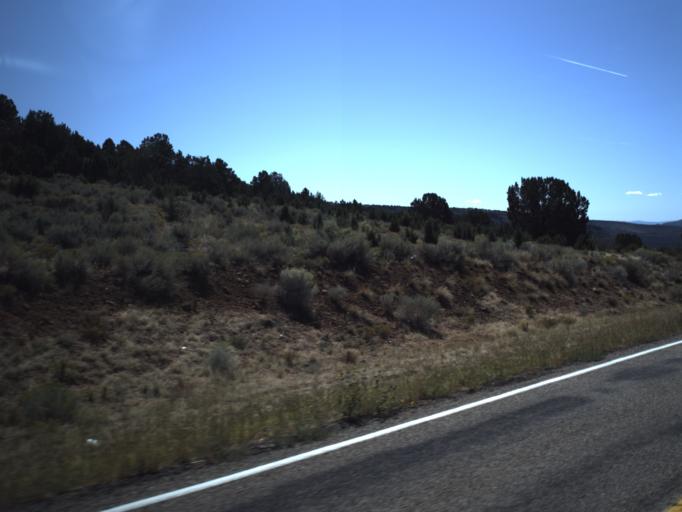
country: US
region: Utah
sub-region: Washington County
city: Enterprise
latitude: 37.3948
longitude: -113.6449
